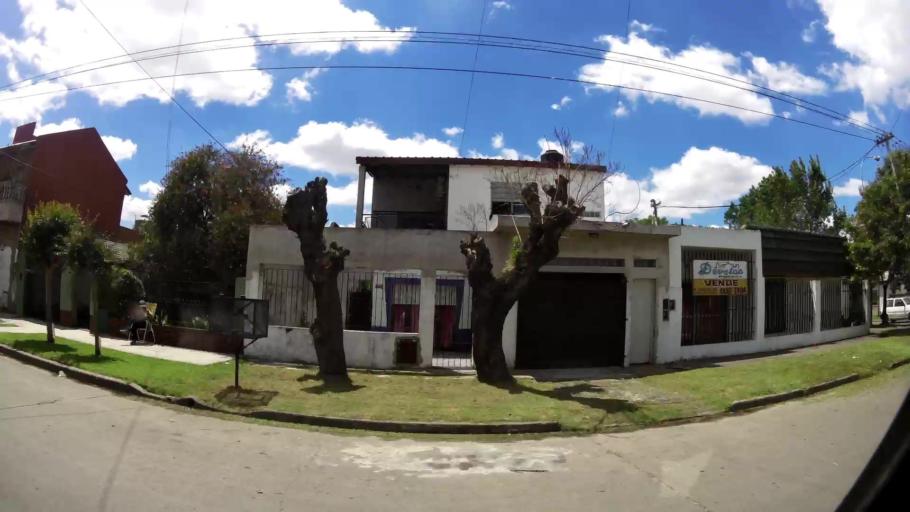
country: AR
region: Buenos Aires
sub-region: Partido de Lanus
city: Lanus
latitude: -34.7133
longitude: -58.4181
